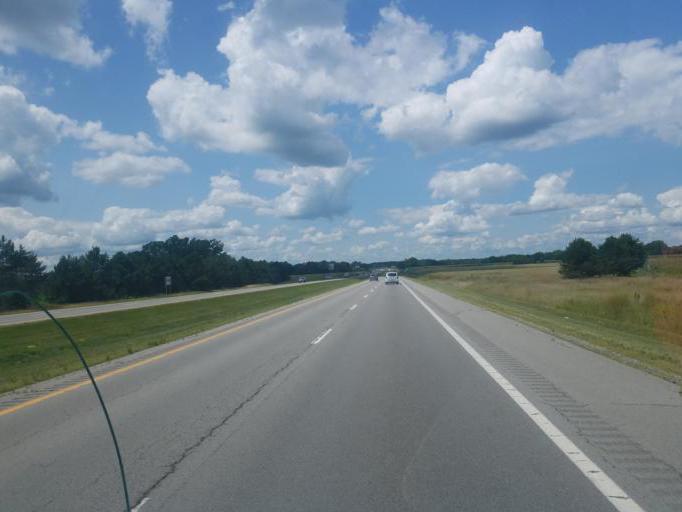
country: US
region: Ohio
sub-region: Wyandot County
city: Upper Sandusky
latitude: 40.7364
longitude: -83.2062
